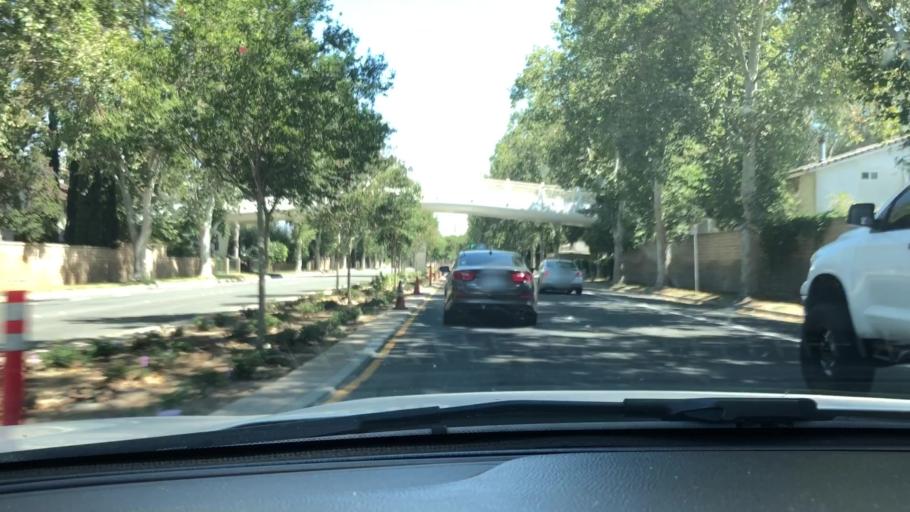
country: US
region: California
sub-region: Los Angeles County
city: Santa Clarita
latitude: 34.3942
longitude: -118.5514
